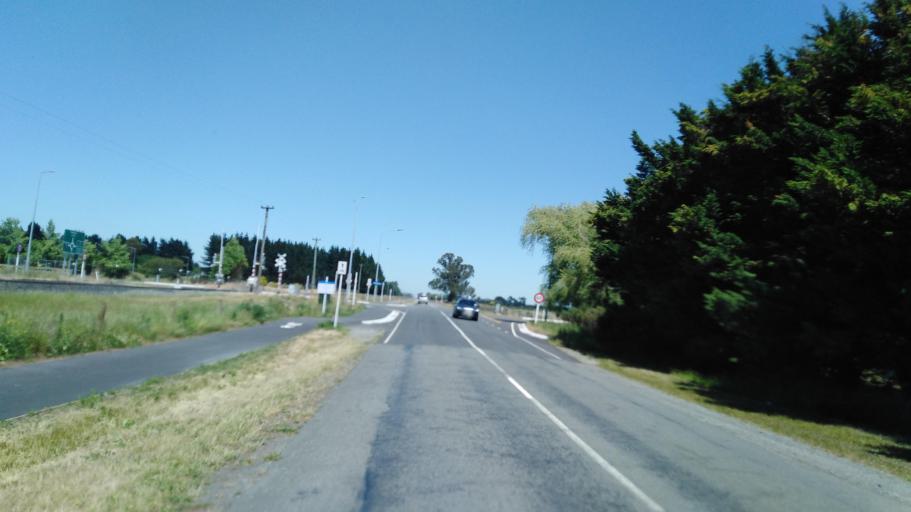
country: NZ
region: Canterbury
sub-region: Selwyn District
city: Prebbleton
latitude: -43.5600
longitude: 172.4586
